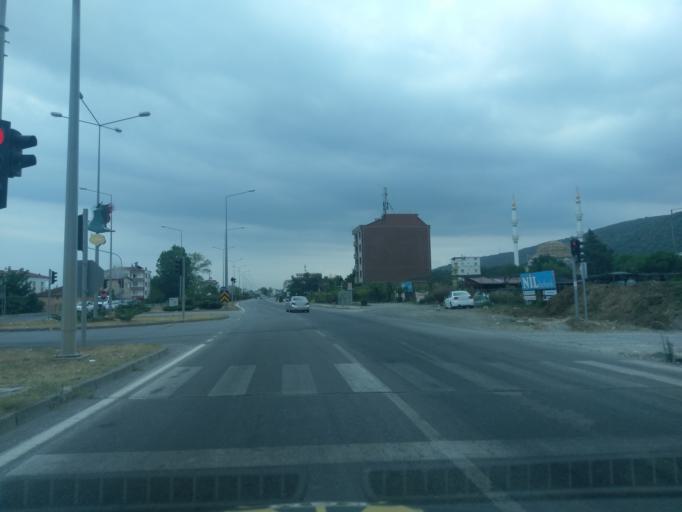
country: TR
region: Samsun
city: Taflan
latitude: 41.4039
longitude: 36.1854
